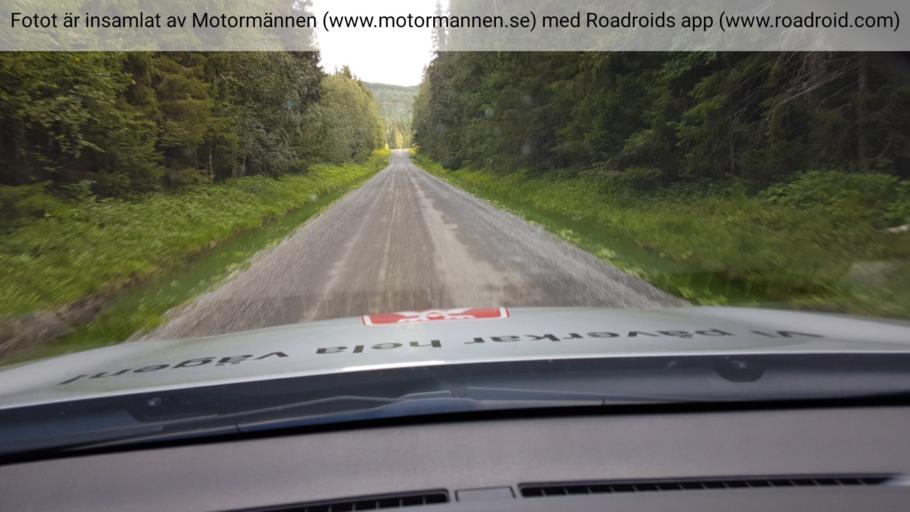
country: SE
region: Jaemtland
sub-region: Ragunda Kommun
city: Hammarstrand
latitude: 63.3159
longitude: 16.0067
